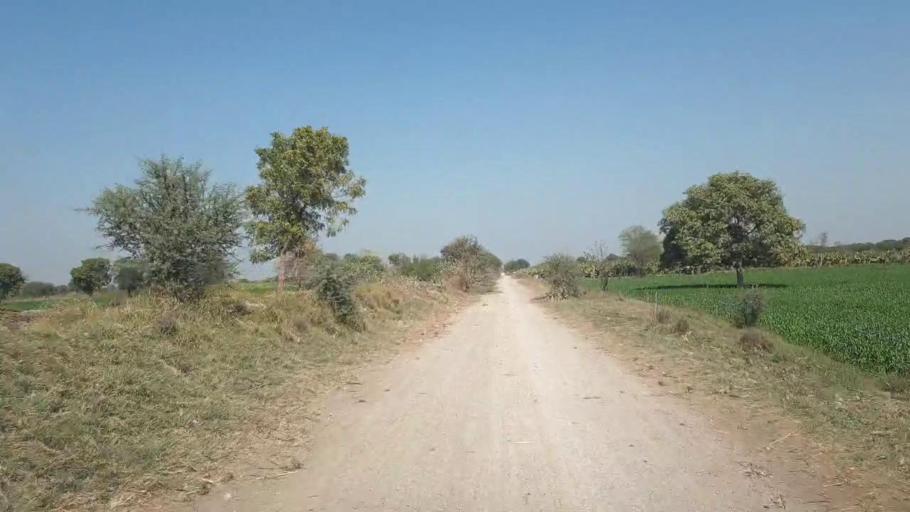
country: PK
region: Sindh
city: Chambar
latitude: 25.3037
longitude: 68.6938
